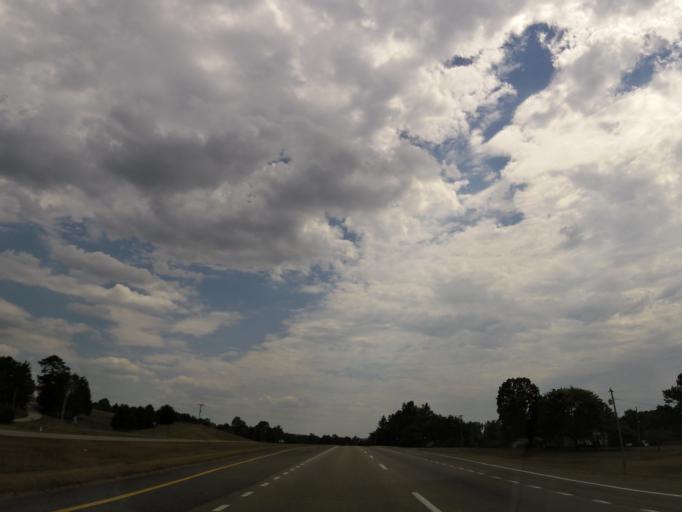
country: US
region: Alabama
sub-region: Jackson County
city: Bridgeport
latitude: 34.9471
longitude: -85.7515
